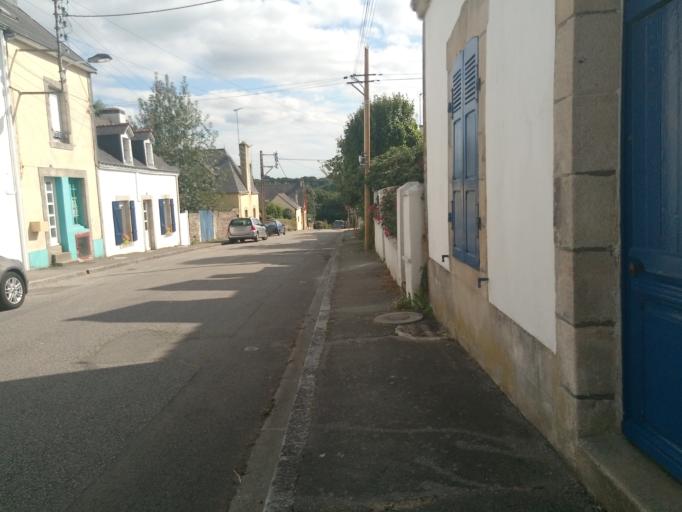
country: FR
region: Brittany
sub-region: Departement du Morbihan
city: Gourin
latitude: 48.1389
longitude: -3.6054
